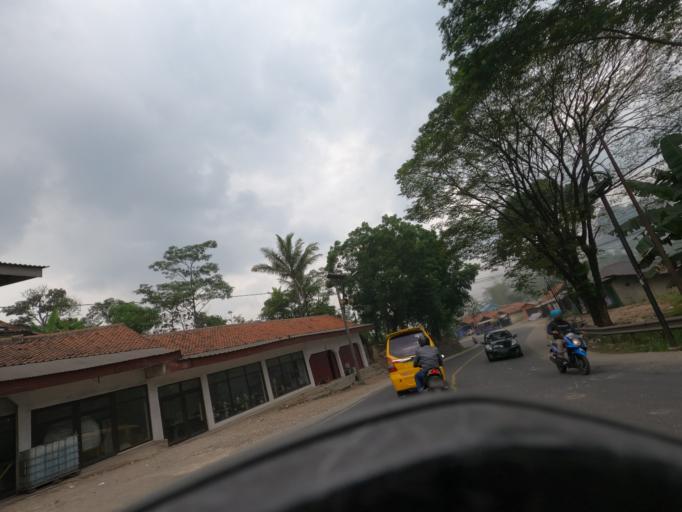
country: ID
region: West Java
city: Padalarang
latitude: -6.8317
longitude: 107.4400
